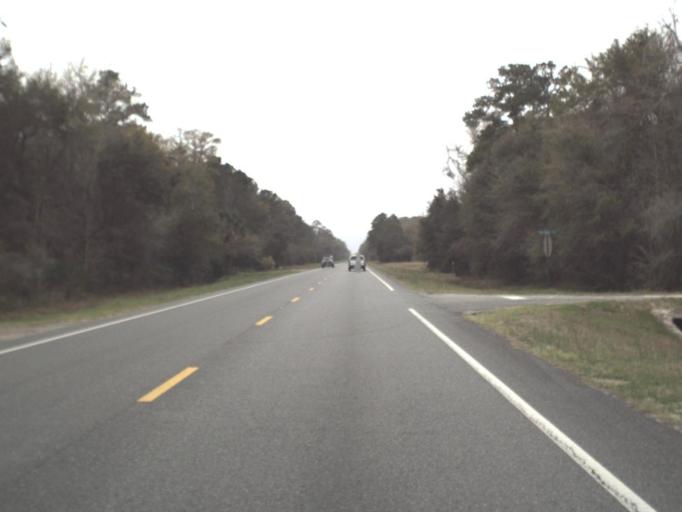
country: US
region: Florida
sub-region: Wakulla County
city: Crawfordville
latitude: 30.1536
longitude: -84.2672
